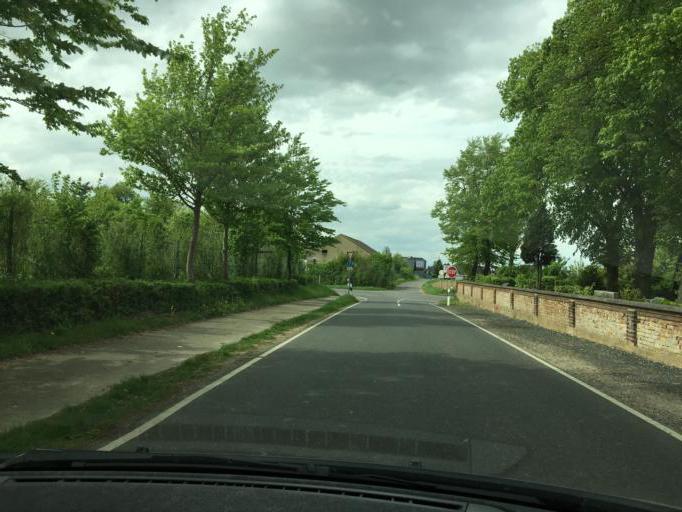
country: DE
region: North Rhine-Westphalia
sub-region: Regierungsbezirk Koln
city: Merzenich
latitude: 50.7936
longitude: 6.5447
